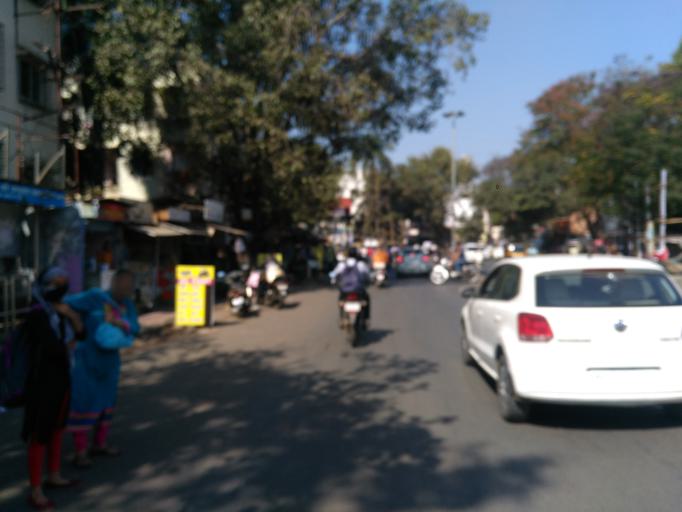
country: IN
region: Maharashtra
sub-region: Pune Division
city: Pune
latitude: 18.4921
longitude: 73.8498
